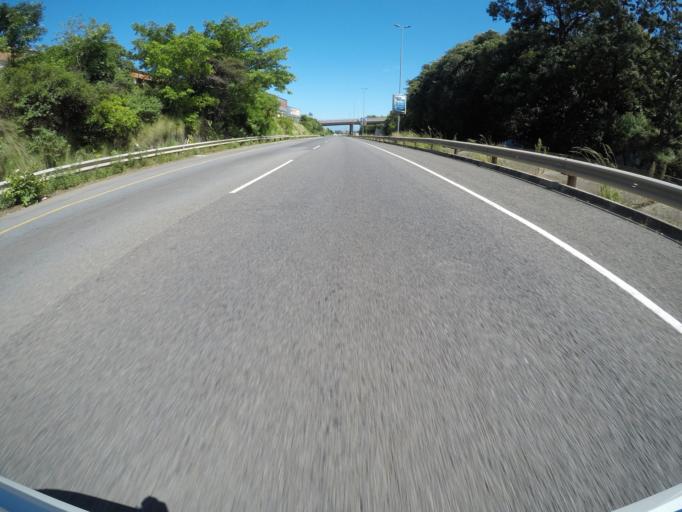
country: ZA
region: Eastern Cape
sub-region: Buffalo City Metropolitan Municipality
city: East London
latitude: -32.9841
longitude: 27.9192
